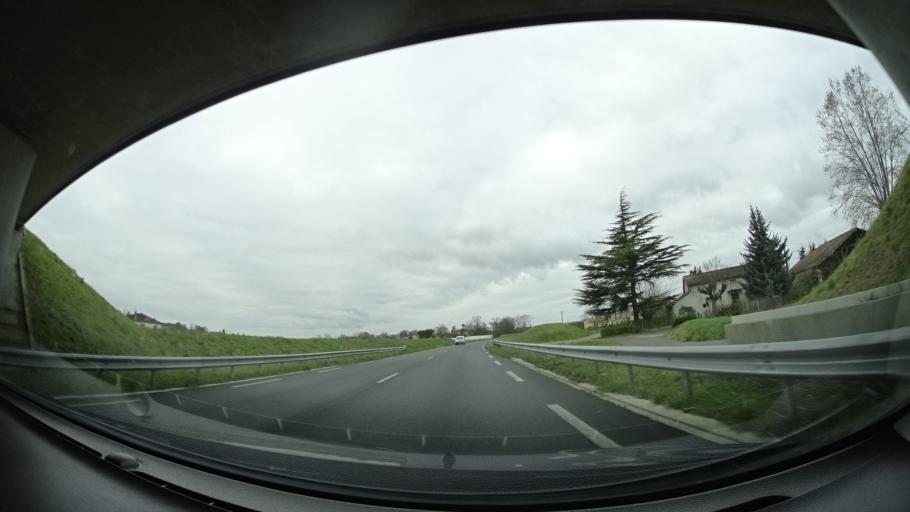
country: FR
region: Aquitaine
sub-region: Departement du Lot-et-Garonne
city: Pujols
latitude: 44.3976
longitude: 0.6816
